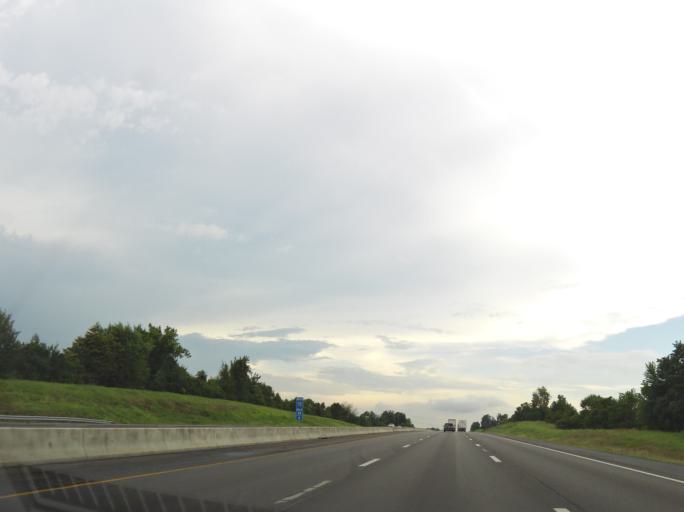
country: US
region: Kentucky
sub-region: Madison County
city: Richmond
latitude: 37.6962
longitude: -84.3164
